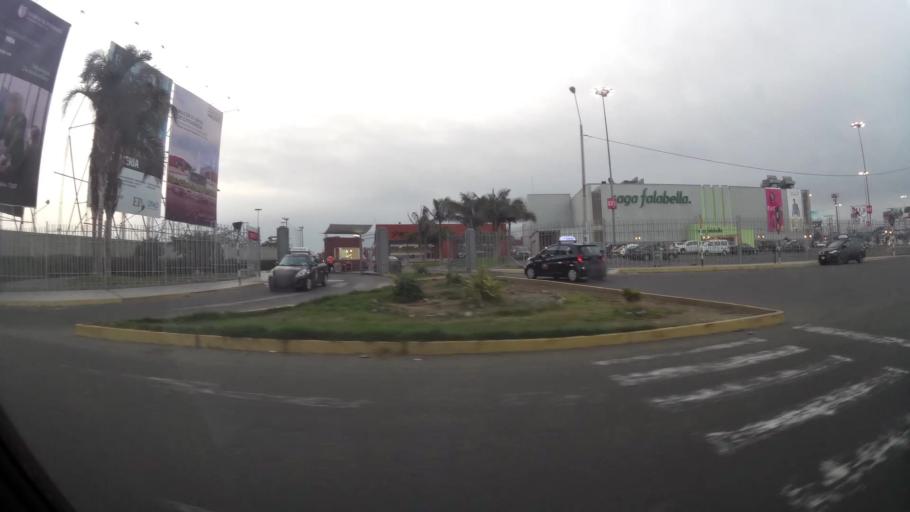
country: PE
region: La Libertad
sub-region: Provincia de Trujillo
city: Trujillo
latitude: -8.1039
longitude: -79.0460
